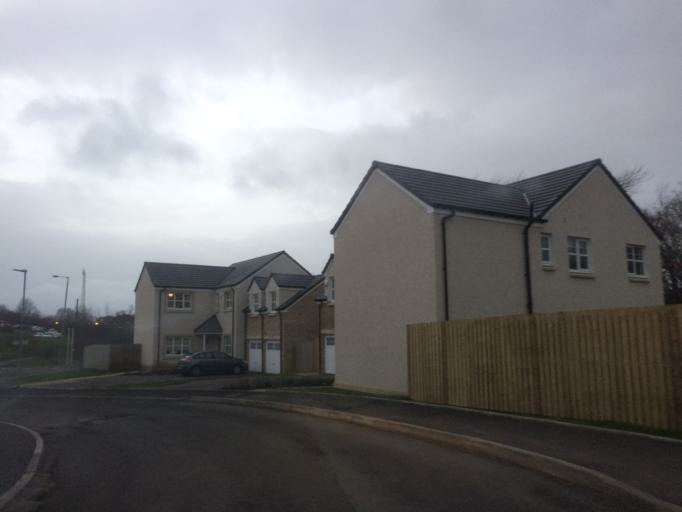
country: GB
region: Scotland
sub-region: East Renfrewshire
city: Newton Mearns
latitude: 55.7902
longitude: -4.3299
